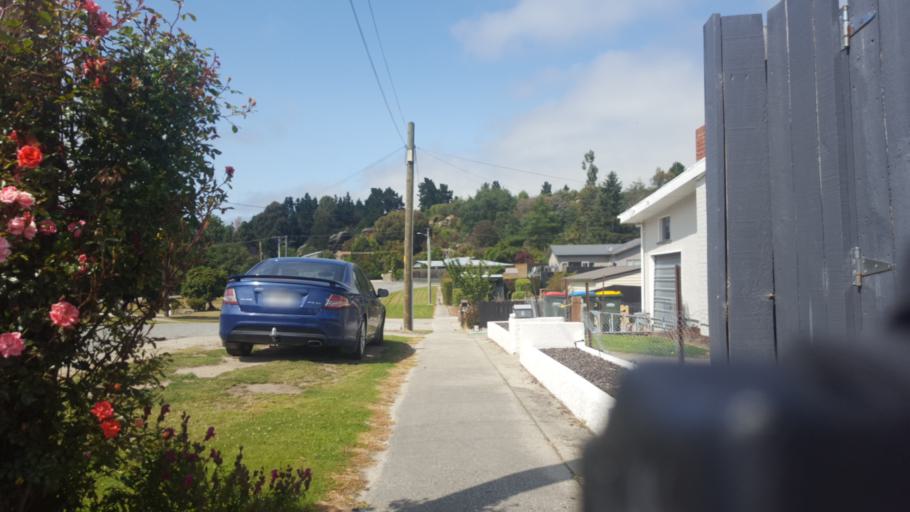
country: NZ
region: Otago
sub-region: Queenstown-Lakes District
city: Kingston
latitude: -45.5427
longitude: 169.3181
